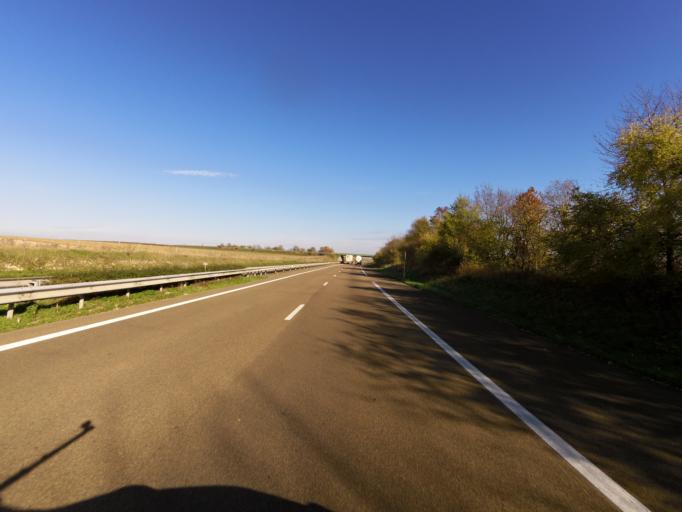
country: FR
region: Champagne-Ardenne
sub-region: Departement de la Marne
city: Fagnieres
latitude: 48.9753
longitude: 4.2854
